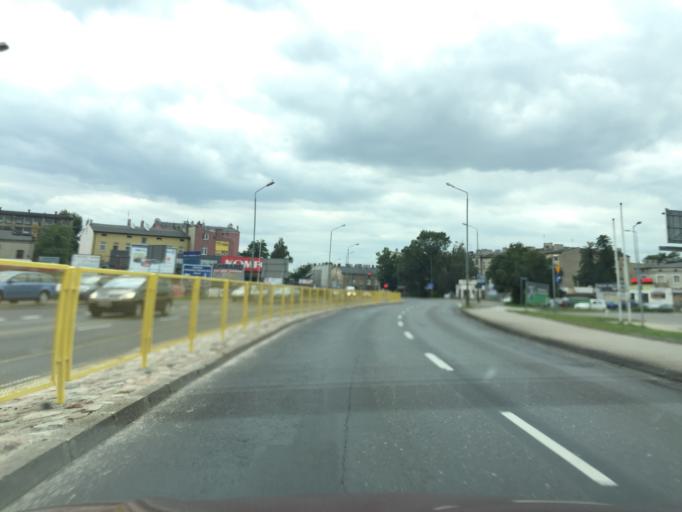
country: PL
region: Greater Poland Voivodeship
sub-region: Kalisz
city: Kalisz
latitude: 51.7669
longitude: 18.0843
